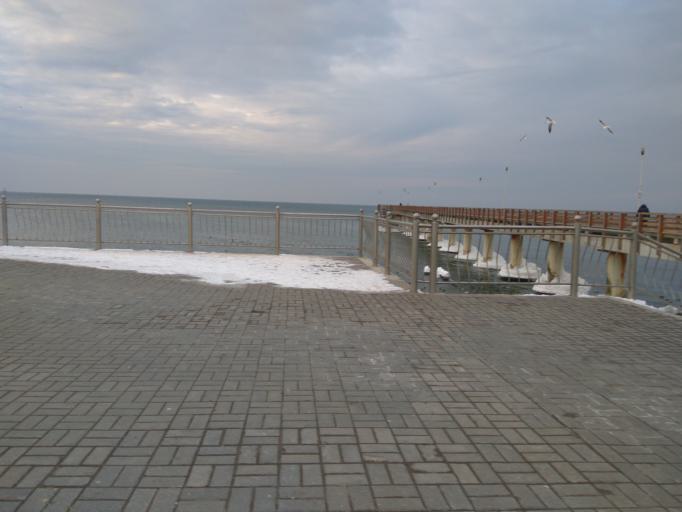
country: RU
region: Kaliningrad
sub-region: Zelenogradskiy Rayon
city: Zelenogradsk
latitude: 54.9620
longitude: 20.4746
